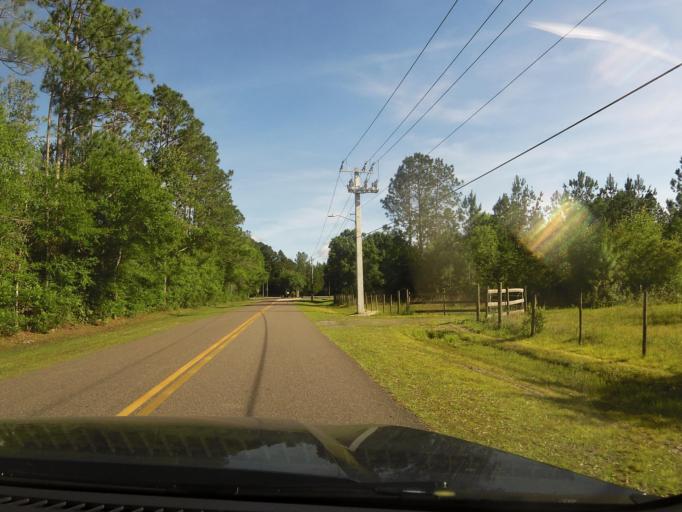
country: US
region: Florida
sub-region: Nassau County
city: Callahan
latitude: 30.5515
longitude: -81.7921
